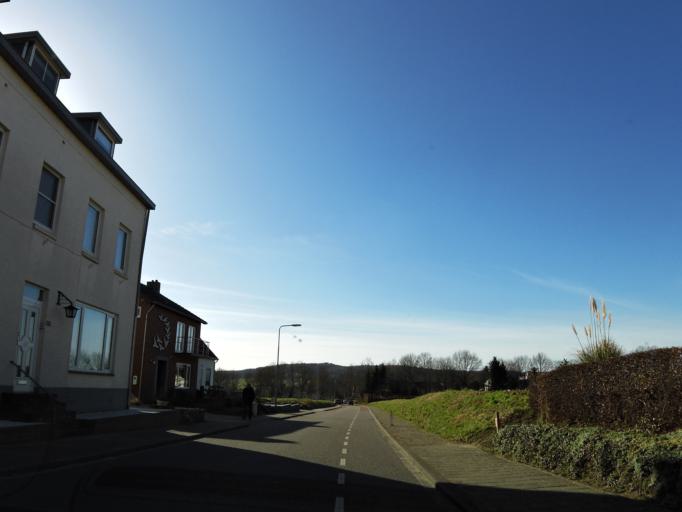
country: NL
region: Limburg
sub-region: Gemeente Voerendaal
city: Ubachsberg
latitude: 50.7978
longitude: 5.9329
